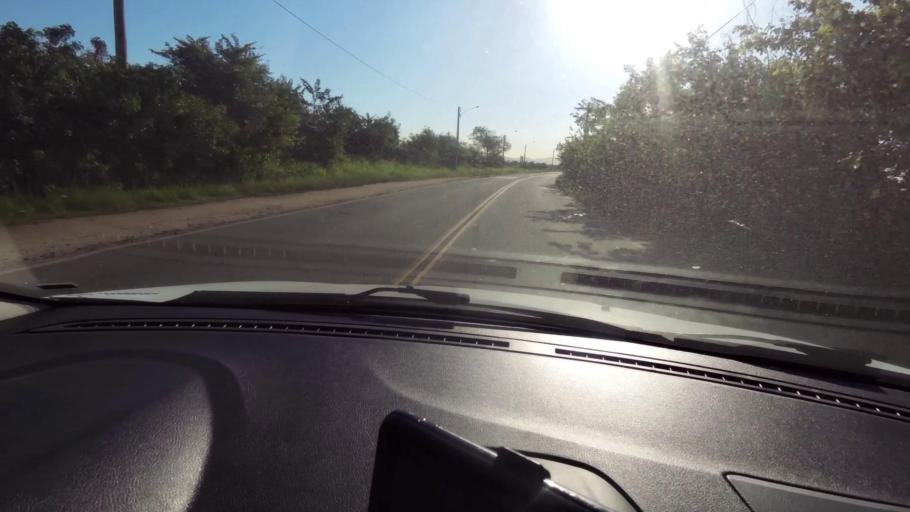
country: BR
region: Espirito Santo
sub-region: Piuma
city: Piuma
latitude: -20.7977
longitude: -40.5985
